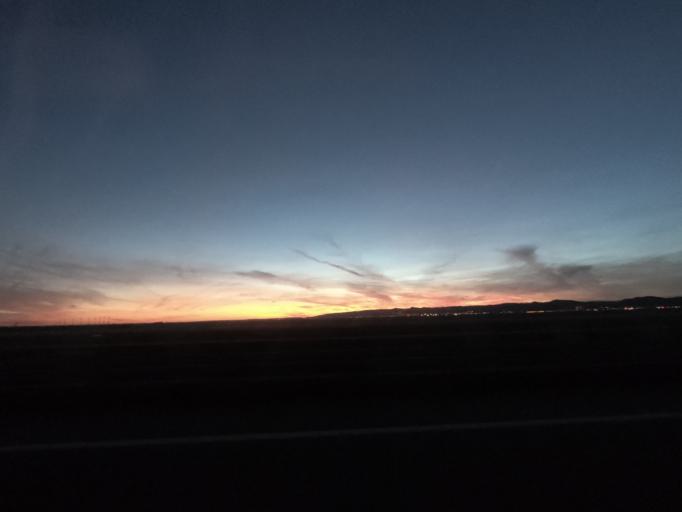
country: PT
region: Santarem
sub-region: Benavente
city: Samora Correia
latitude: 38.9976
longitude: -8.9016
